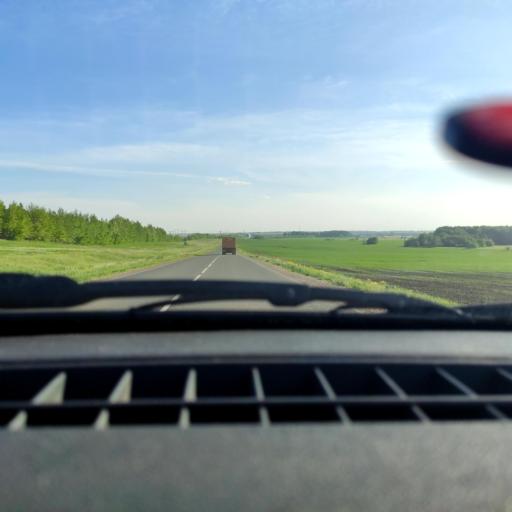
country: RU
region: Bashkortostan
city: Avdon
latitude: 54.4499
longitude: 55.8464
